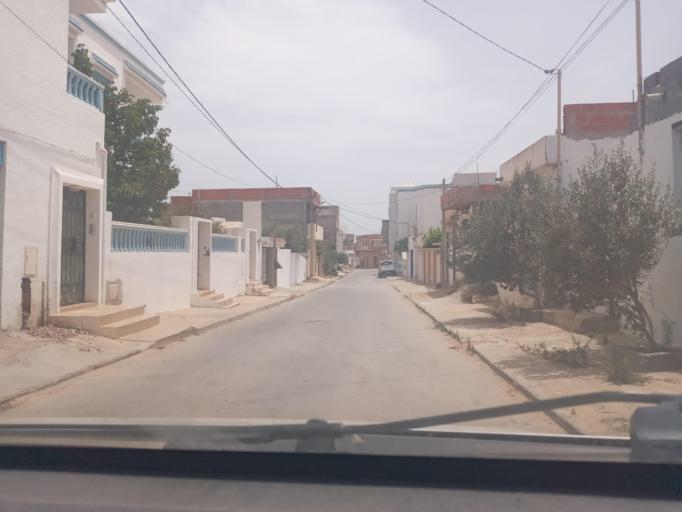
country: TN
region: Nabul
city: El Haouaria
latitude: 37.0527
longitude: 11.0109
